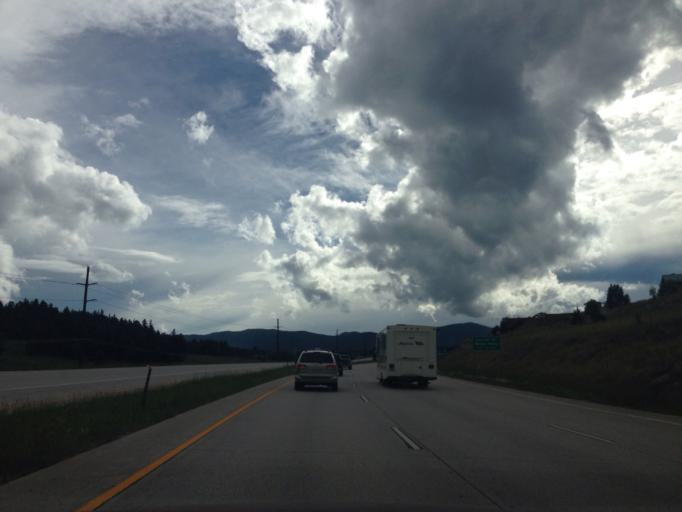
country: US
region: Colorado
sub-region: Jefferson County
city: Indian Hills
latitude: 39.5438
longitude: -105.2834
